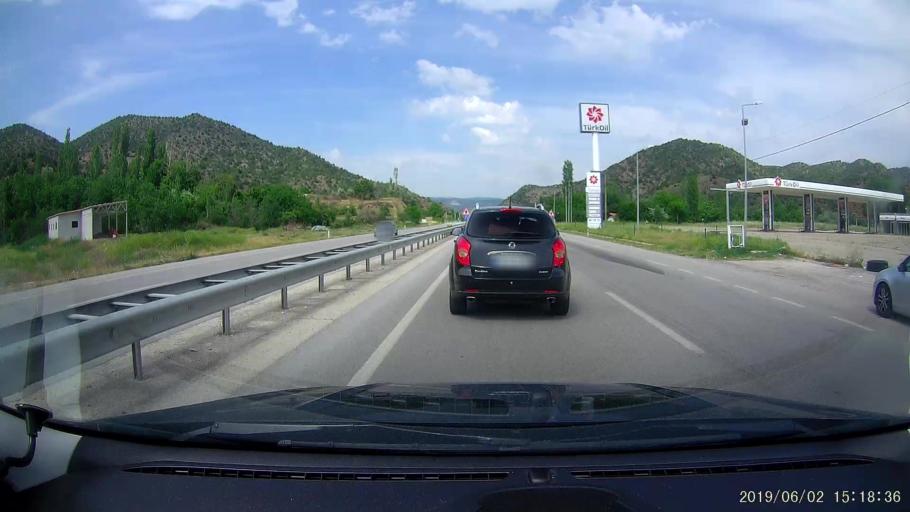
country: TR
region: Corum
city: Osmancik
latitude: 40.9632
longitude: 34.8991
